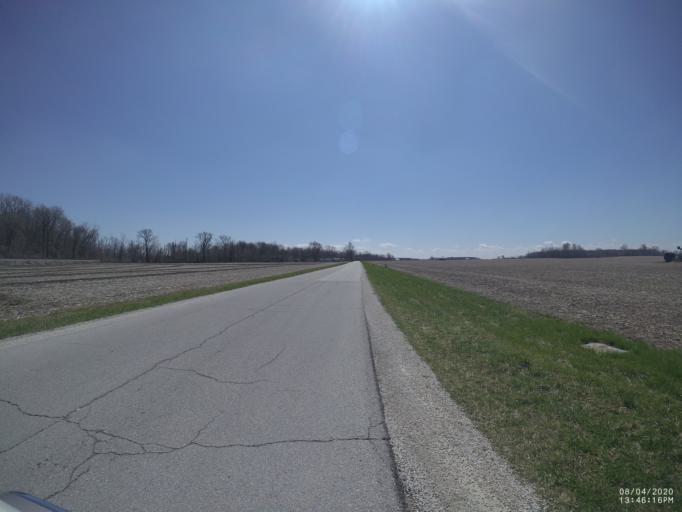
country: US
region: Ohio
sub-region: Sandusky County
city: Gibsonburg
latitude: 41.3263
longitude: -83.2869
